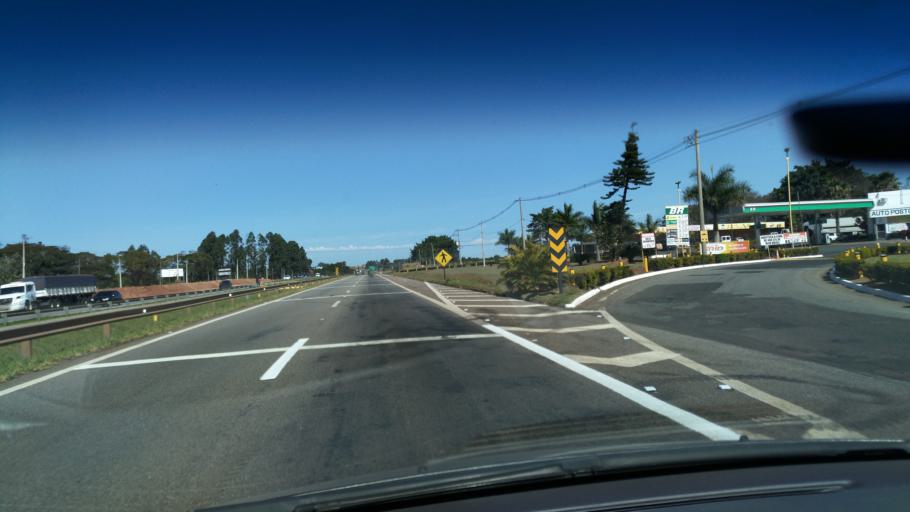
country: BR
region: Sao Paulo
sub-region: Santo Antonio De Posse
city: Santo Antonio de Posse
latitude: -22.6089
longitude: -47.0075
